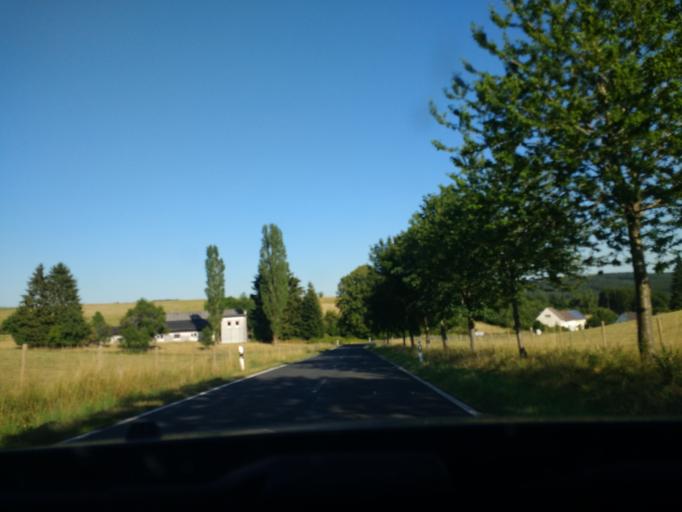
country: DE
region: Rheinland-Pfalz
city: Meisburg
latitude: 50.1077
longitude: 6.7004
